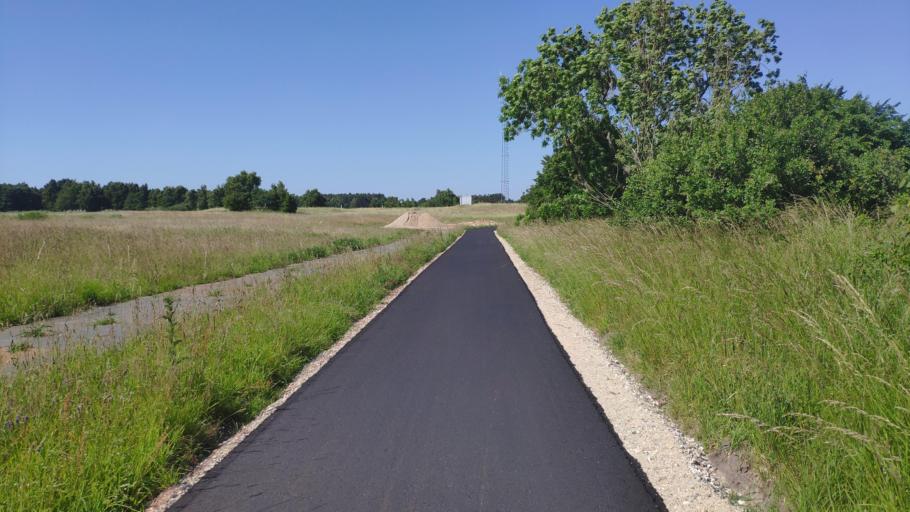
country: DK
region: Capital Region
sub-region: Frederikssund Kommune
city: Jaegerspris
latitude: 55.8863
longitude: 11.9545
